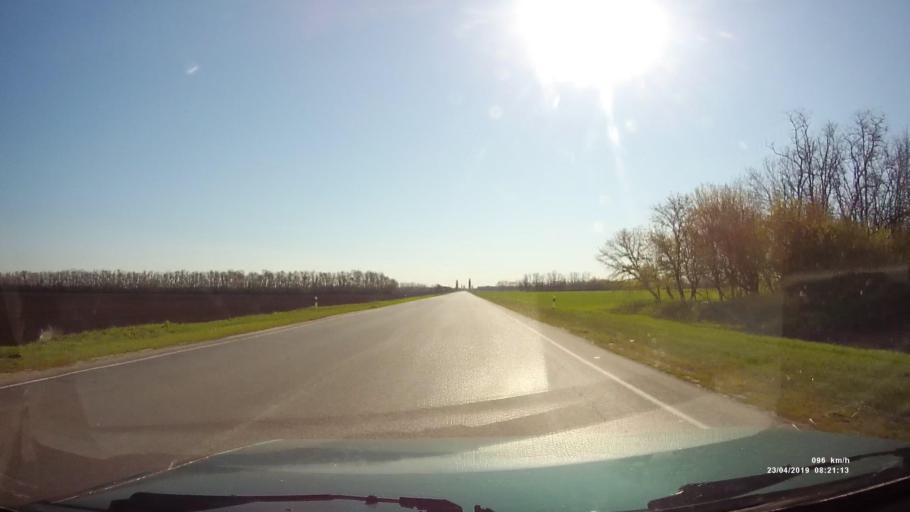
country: RU
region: Rostov
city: Tselina
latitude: 46.5357
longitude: 40.8858
